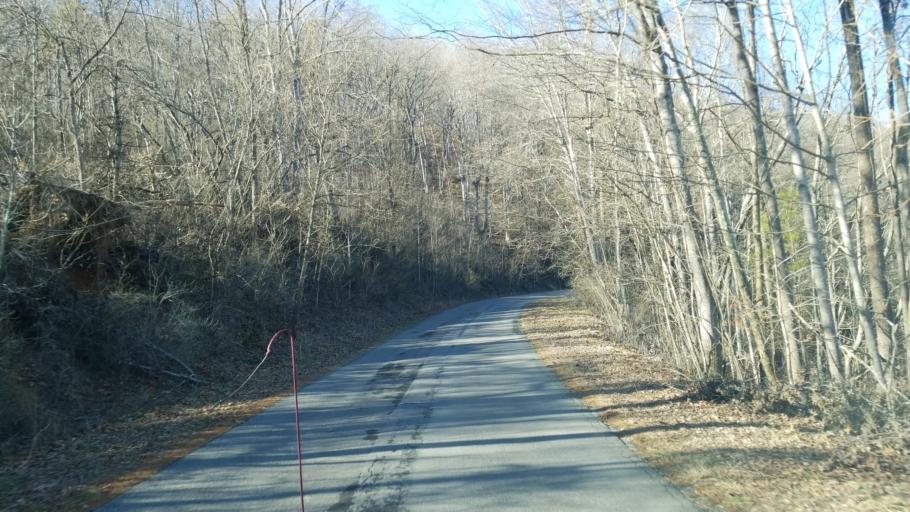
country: US
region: Virginia
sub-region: Pulaski County
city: Pulaski
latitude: 37.1646
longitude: -80.8593
